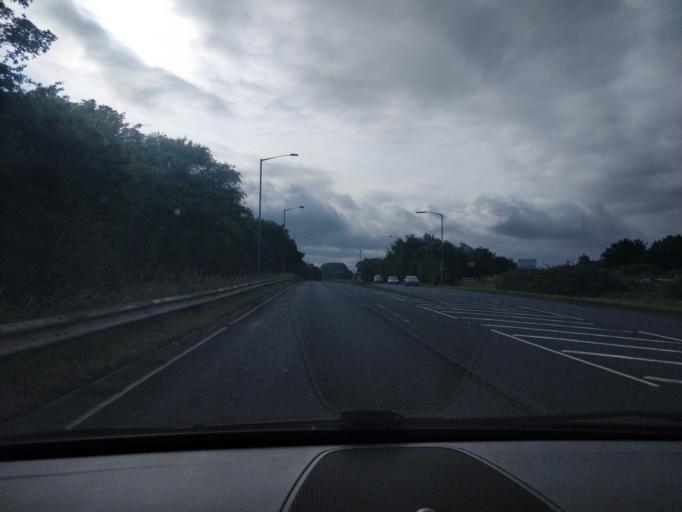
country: GB
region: England
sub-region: Lancashire
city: Banks
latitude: 53.6751
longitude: -2.9320
